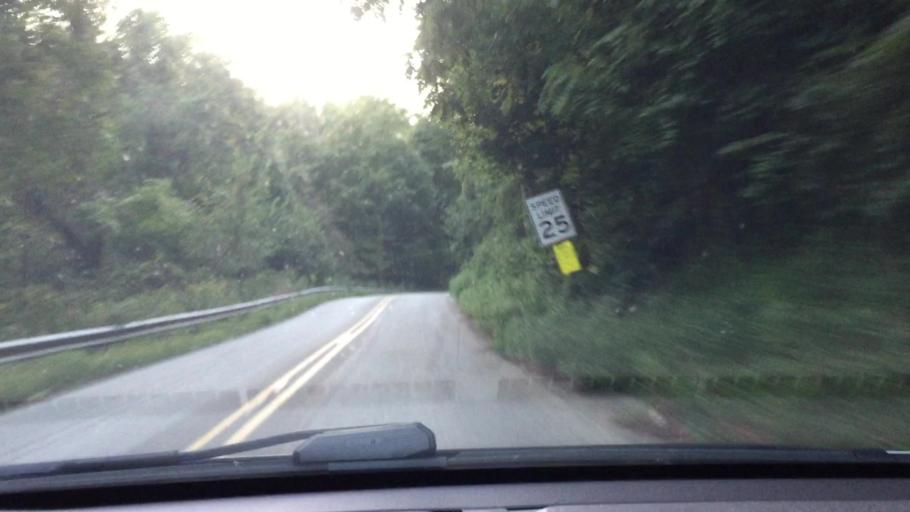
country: US
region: Pennsylvania
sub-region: Washington County
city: Thompsonville
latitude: 40.2673
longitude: -80.1407
